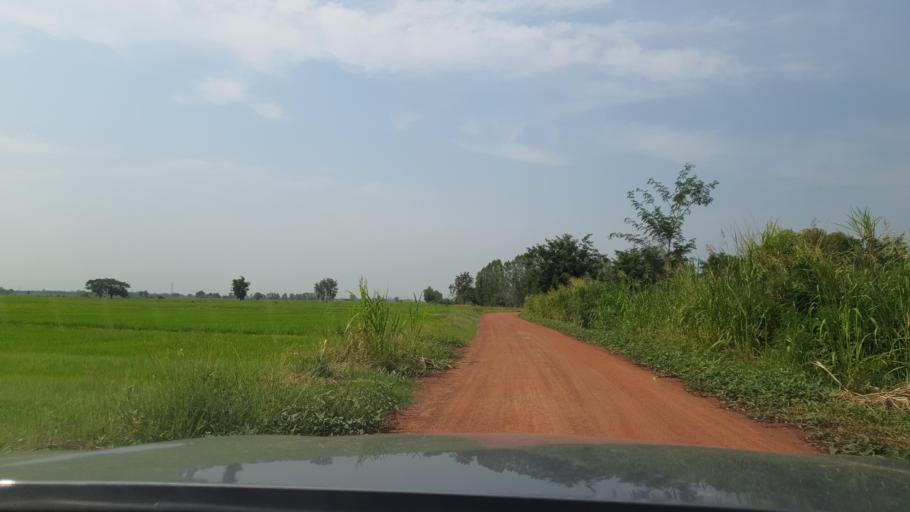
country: TH
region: Phitsanulok
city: Bang Rakam
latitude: 16.7981
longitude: 100.1074
